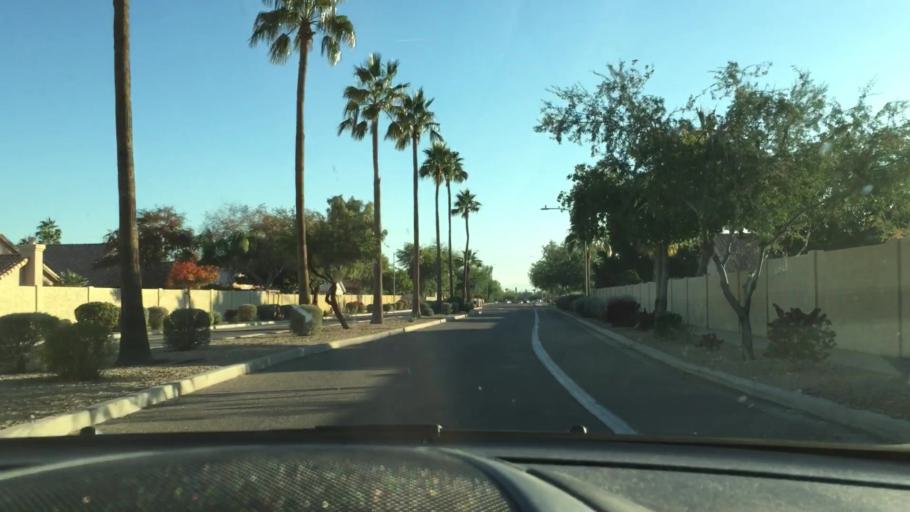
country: US
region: Arizona
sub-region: Maricopa County
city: Sun City
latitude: 33.6563
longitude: -112.2291
